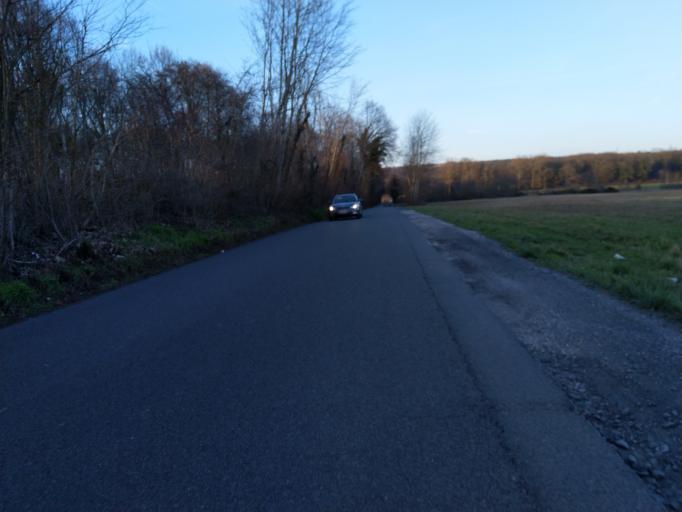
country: BE
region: Wallonia
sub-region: Province du Hainaut
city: Mons
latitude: 50.4862
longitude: 3.9488
